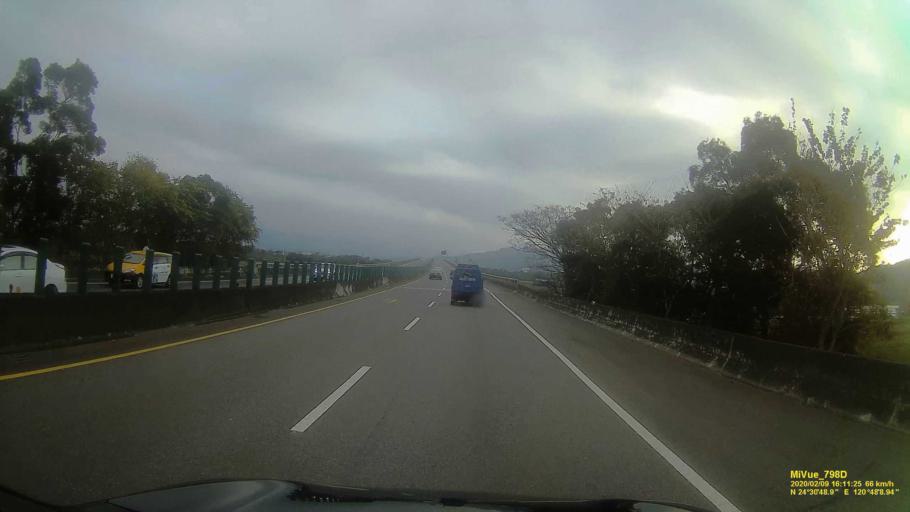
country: TW
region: Taiwan
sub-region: Miaoli
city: Miaoli
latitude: 24.5134
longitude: 120.8025
